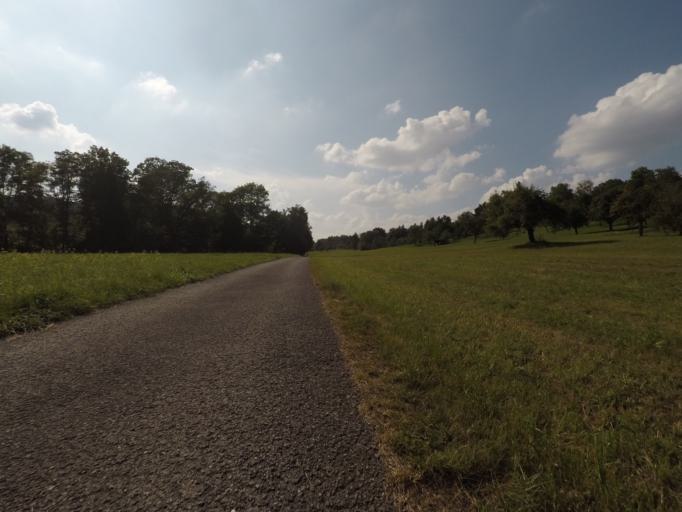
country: DE
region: Baden-Wuerttemberg
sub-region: Regierungsbezirk Stuttgart
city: Weil im Schonbuch
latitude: 48.6177
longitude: 9.0528
